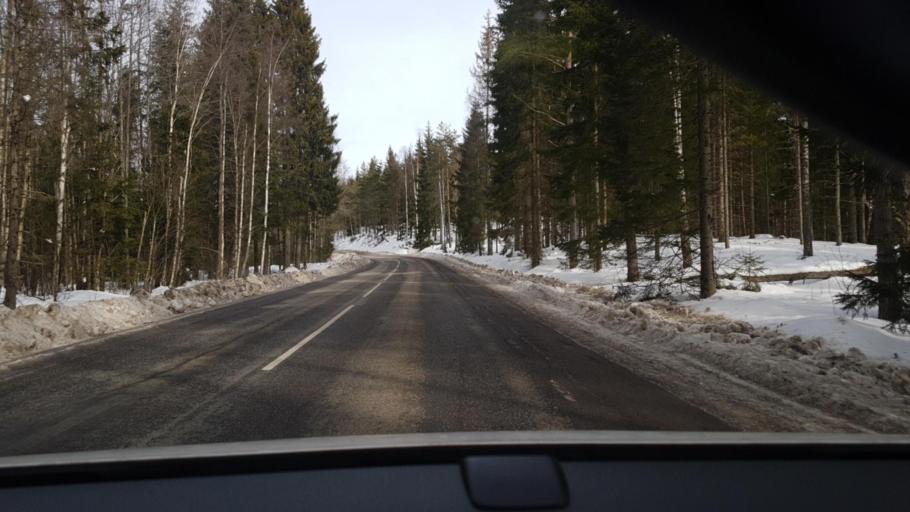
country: SE
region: Vaermland
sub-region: Eda Kommun
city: Amotfors
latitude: 59.6123
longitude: 12.3286
